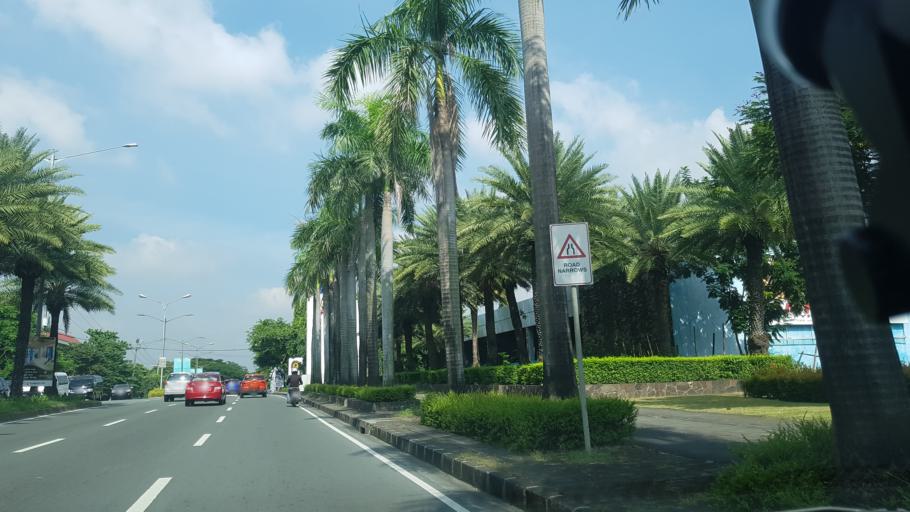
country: PH
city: Sambayanihan People's Village
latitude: 14.4211
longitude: 121.0333
